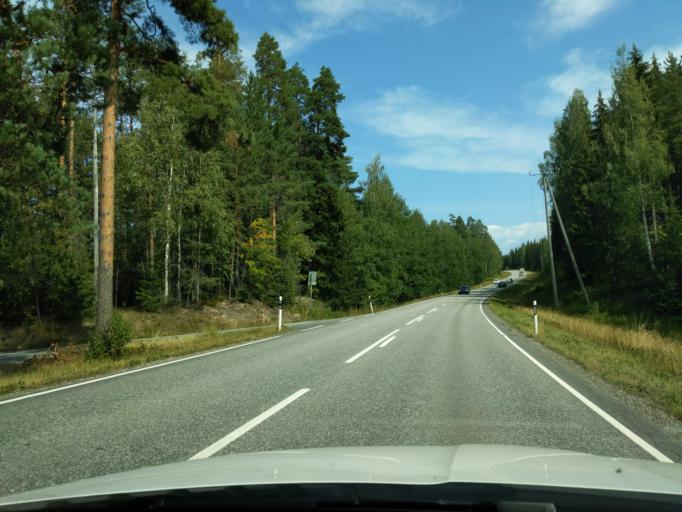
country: FI
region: Paijanne Tavastia
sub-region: Lahti
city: Padasjoki
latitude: 61.3295
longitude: 25.2026
